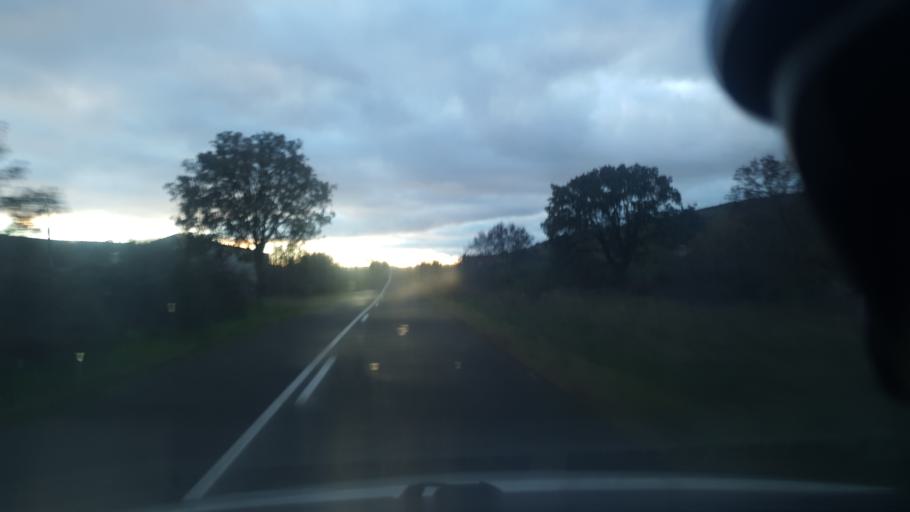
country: ES
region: Castille and Leon
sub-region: Provincia de Segovia
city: Vegas de Matute
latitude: 40.7174
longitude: -4.3052
